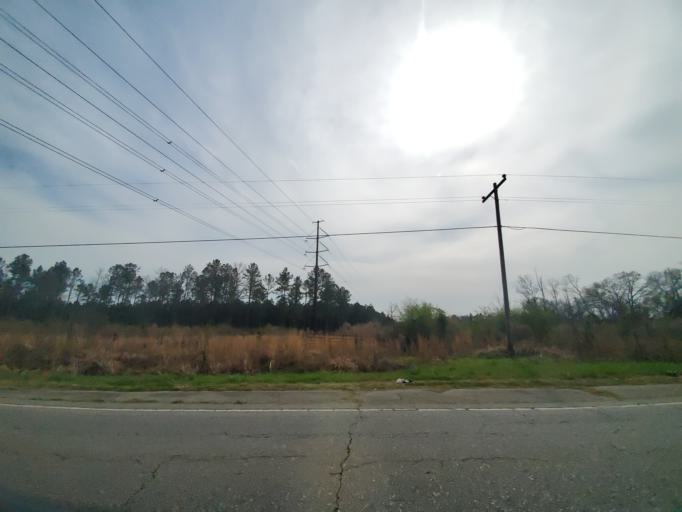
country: US
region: South Carolina
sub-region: Bamberg County
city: Bamberg
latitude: 33.3040
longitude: -81.0613
